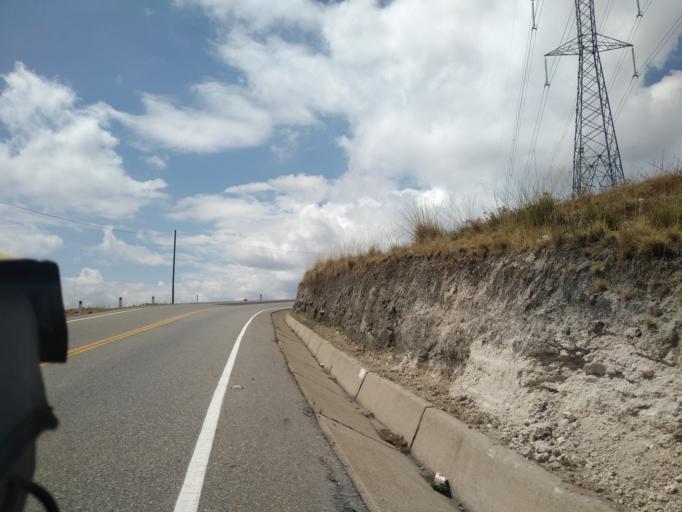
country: PE
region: La Libertad
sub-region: Provincia de Santiago de Chuco
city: Quiruvilca
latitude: -7.9240
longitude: -78.1526
